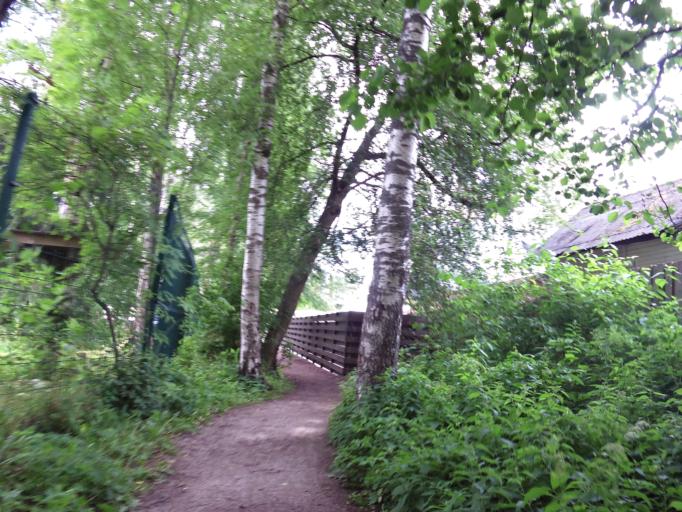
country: EE
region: Harju
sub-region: Saue vald
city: Laagri
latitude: 59.3897
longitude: 24.6549
